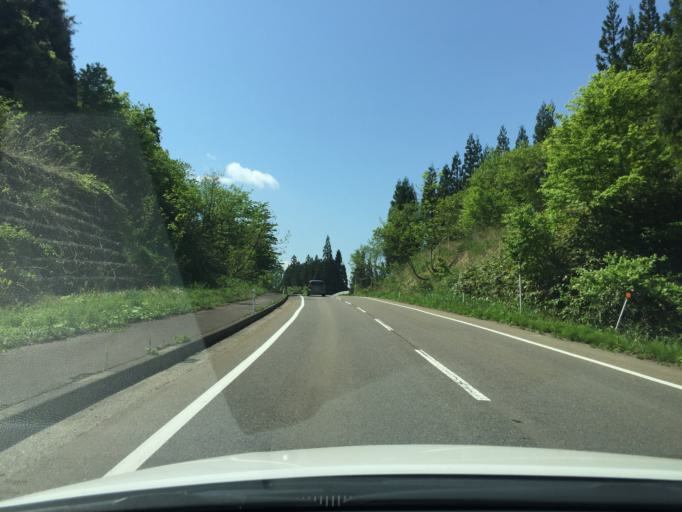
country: JP
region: Niigata
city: Kamo
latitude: 37.5937
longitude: 139.0931
